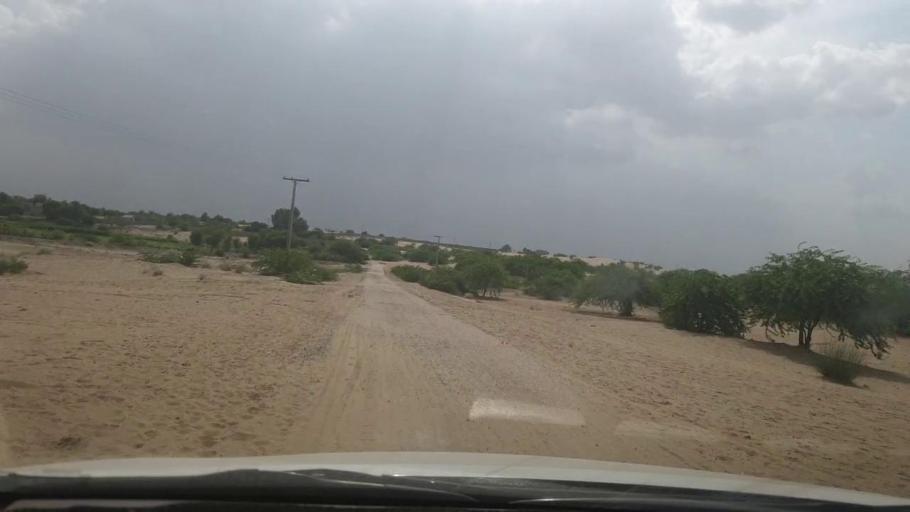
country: PK
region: Sindh
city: Kot Diji
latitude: 27.3399
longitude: 69.0171
